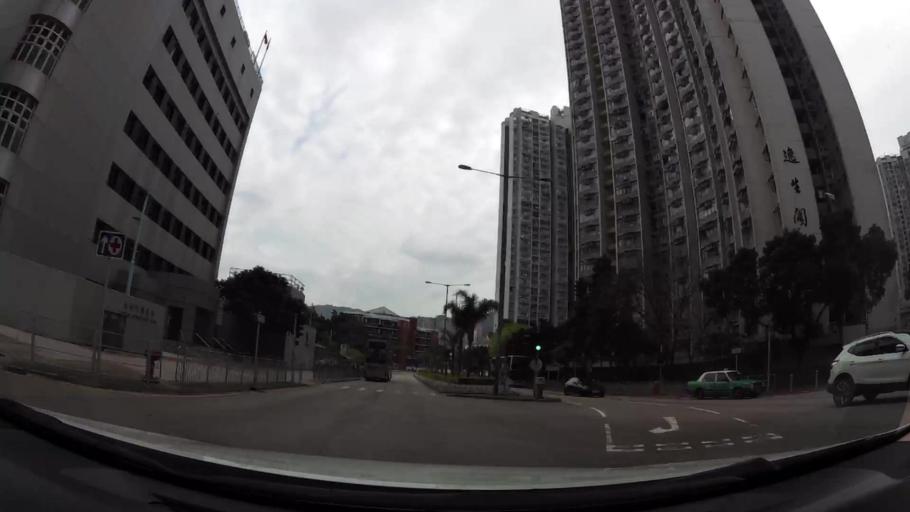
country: HK
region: Tuen Mun
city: Tuen Mun
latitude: 22.4083
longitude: 113.9695
